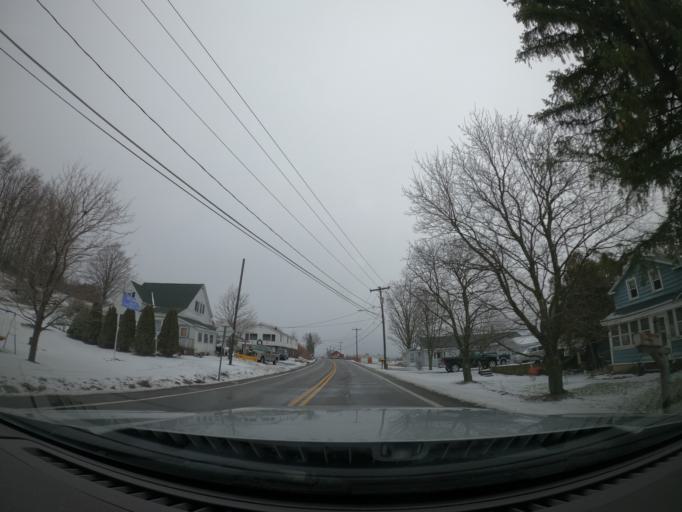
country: US
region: New York
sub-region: Onondaga County
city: Nedrow
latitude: 42.8244
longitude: -76.0513
